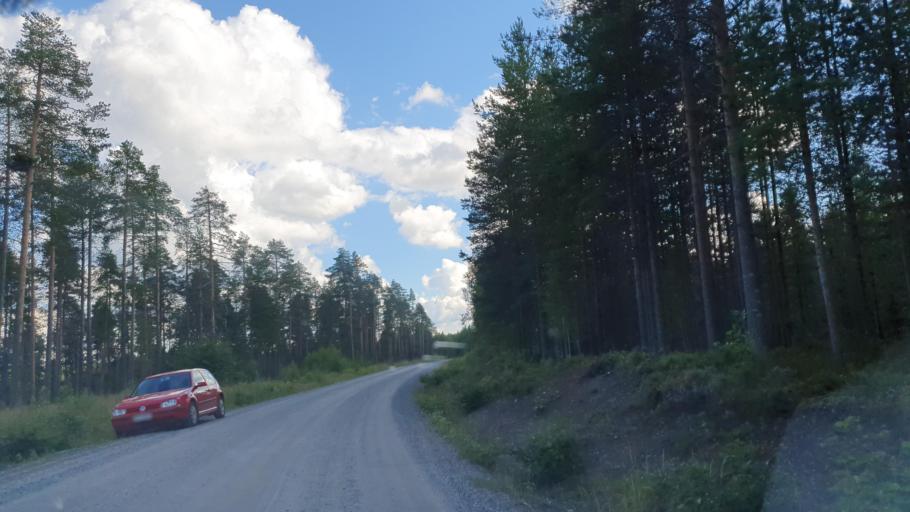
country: FI
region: Kainuu
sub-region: Kehys-Kainuu
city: Kuhmo
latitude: 64.0974
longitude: 29.4112
